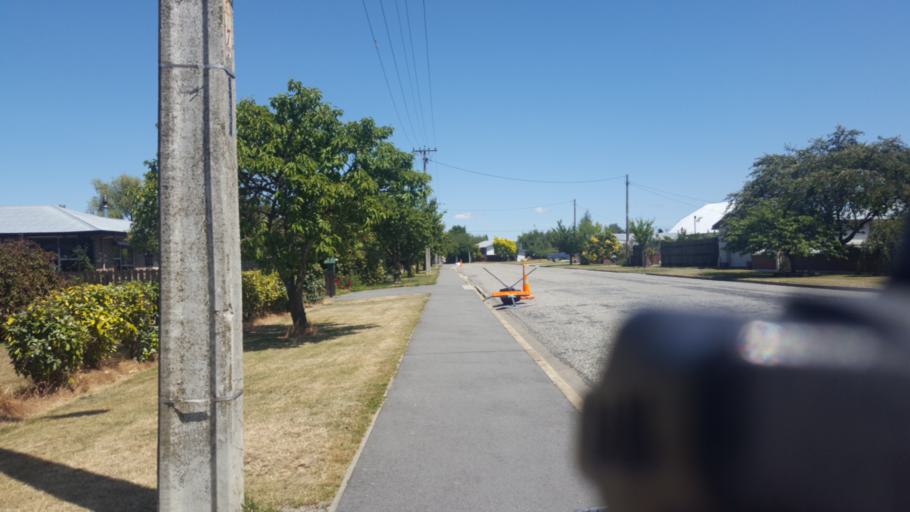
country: NZ
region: Otago
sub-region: Dunedin City
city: Dunedin
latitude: -45.1284
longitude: 170.1080
